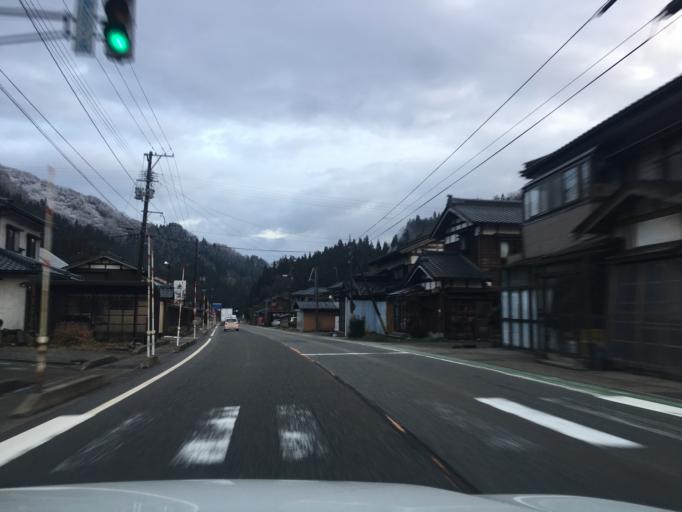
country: JP
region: Niigata
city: Murakami
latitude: 38.3887
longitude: 139.5552
